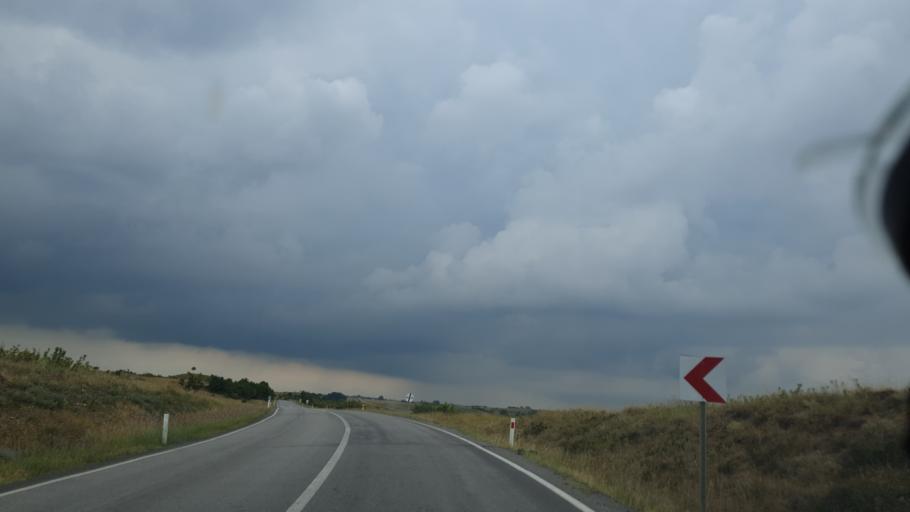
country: TR
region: Tekirdag
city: Hayrabolu
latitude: 41.2218
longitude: 27.0136
